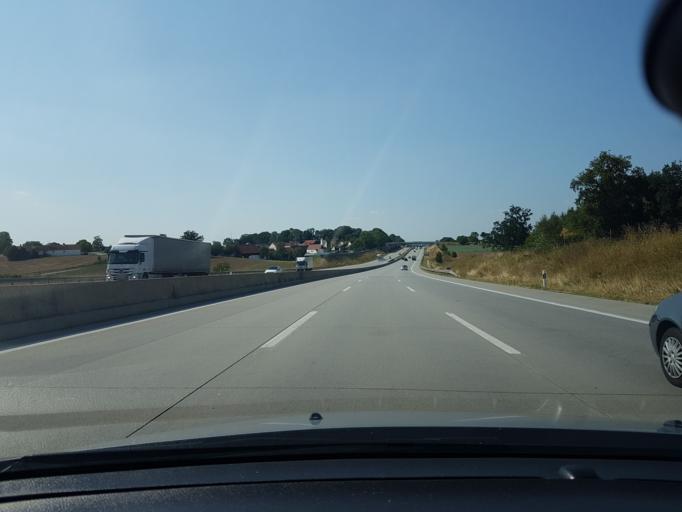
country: DE
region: Bavaria
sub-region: Swabia
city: Adelzhausen
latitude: 48.3706
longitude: 11.1024
